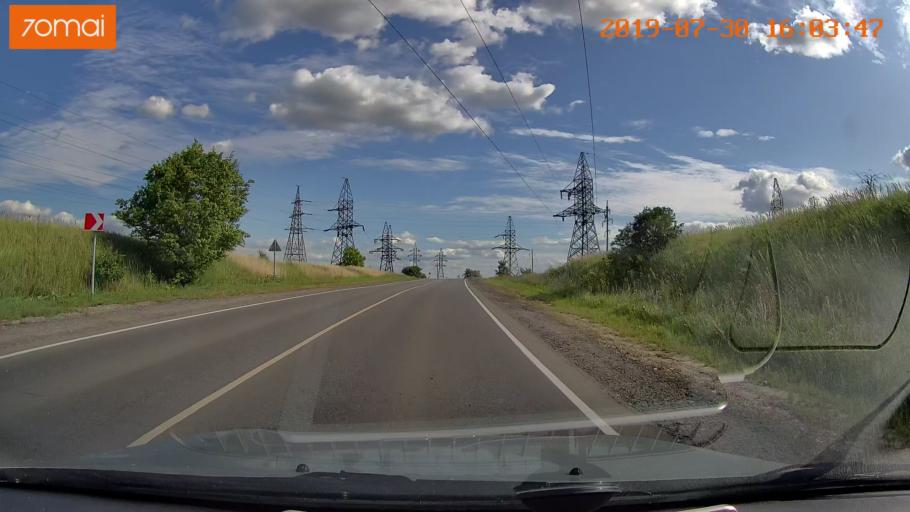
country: RU
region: Moskovskaya
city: Voskresensk
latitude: 55.2875
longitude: 38.6995
